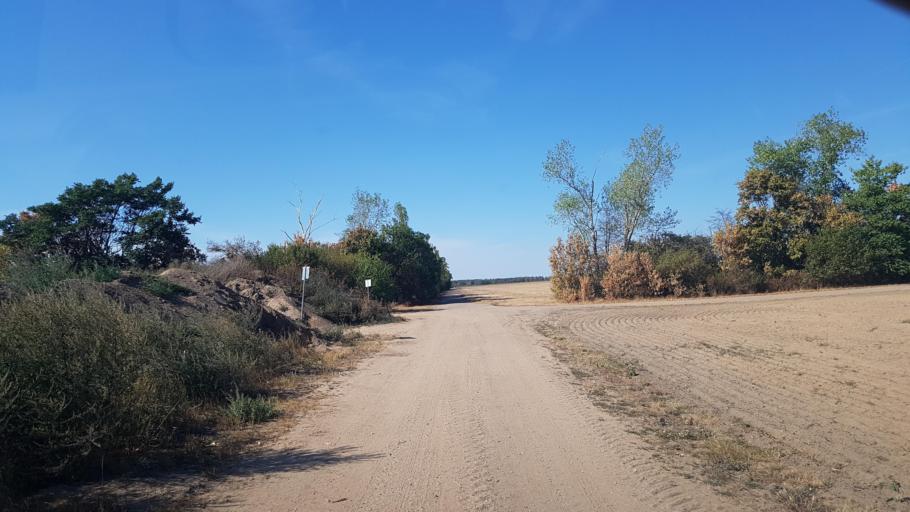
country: DE
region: Brandenburg
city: Muhlberg
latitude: 51.4242
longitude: 13.2866
